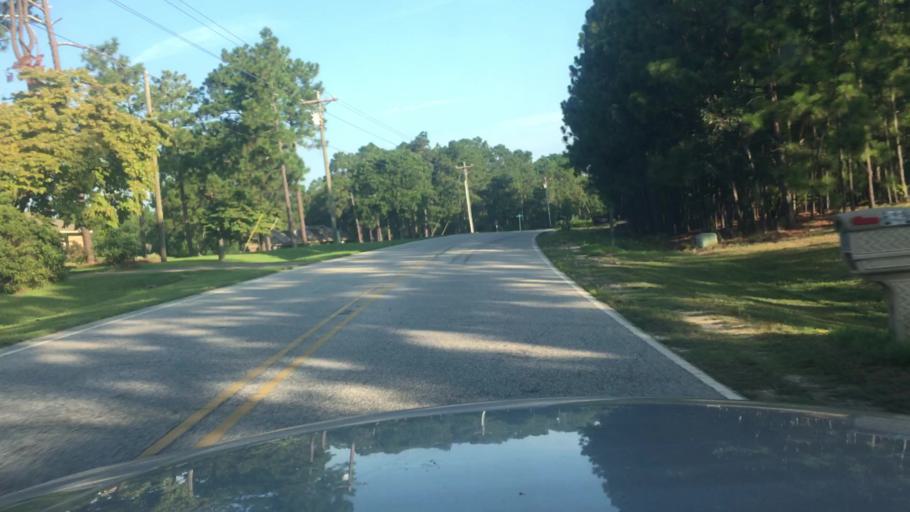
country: US
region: North Carolina
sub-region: Harnett County
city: Walkertown
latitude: 35.2117
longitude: -78.8629
